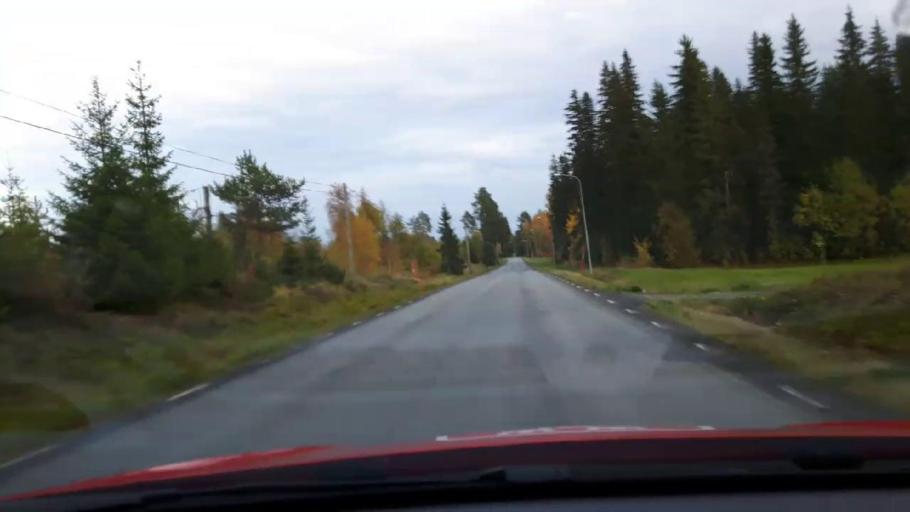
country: SE
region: Jaemtland
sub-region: OEstersunds Kommun
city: Lit
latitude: 63.3172
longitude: 14.9710
